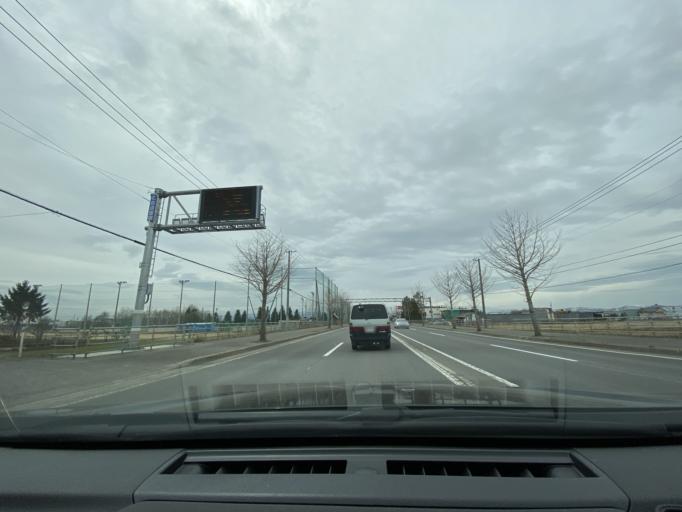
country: JP
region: Hokkaido
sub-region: Asahikawa-shi
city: Asahikawa
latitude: 43.8201
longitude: 142.4095
